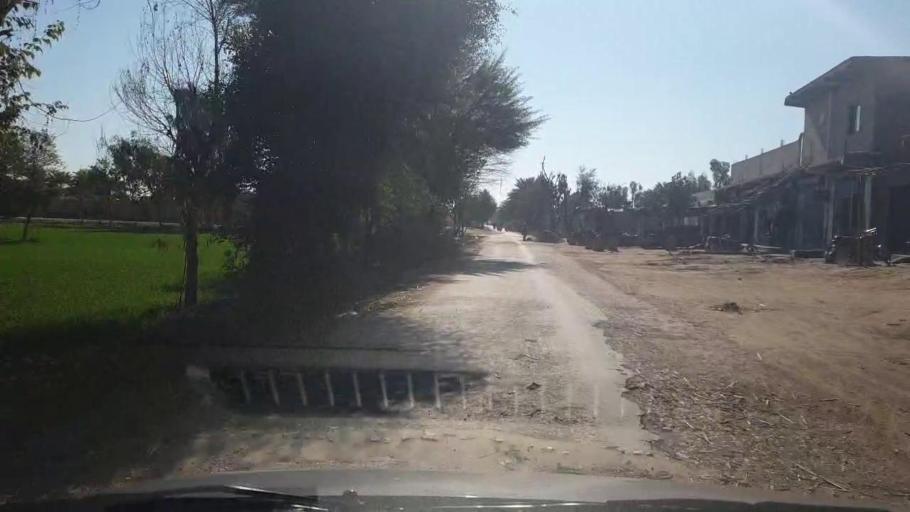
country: PK
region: Sindh
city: Bozdar
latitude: 27.1768
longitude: 68.6400
